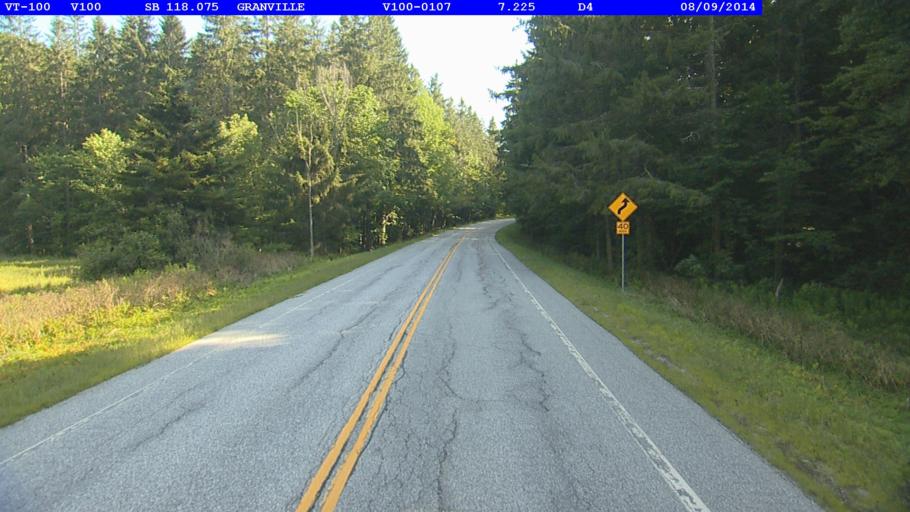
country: US
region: Vermont
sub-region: Orange County
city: Randolph
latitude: 44.0342
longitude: -72.8316
